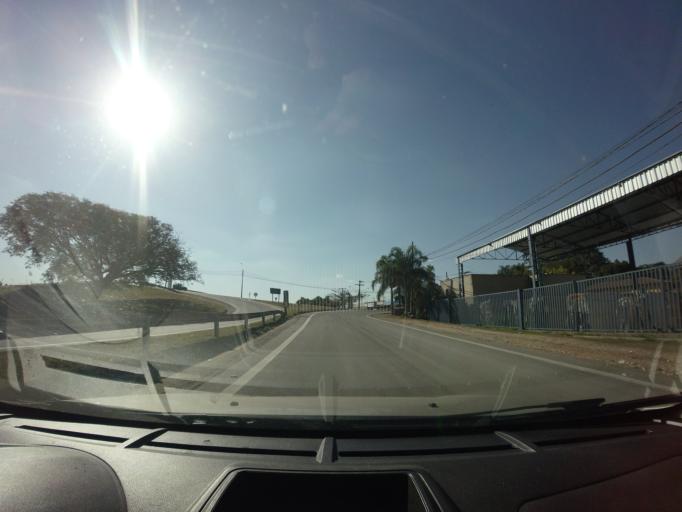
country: BR
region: Sao Paulo
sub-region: Piracicaba
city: Piracicaba
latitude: -22.7430
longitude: -47.5996
